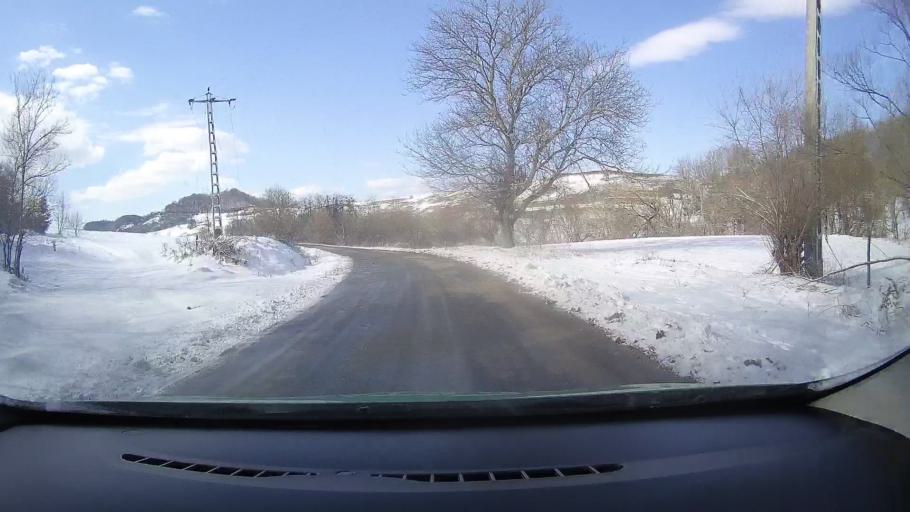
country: RO
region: Sibiu
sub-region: Comuna Mihaileni
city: Mihaileni
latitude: 46.0218
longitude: 24.3969
